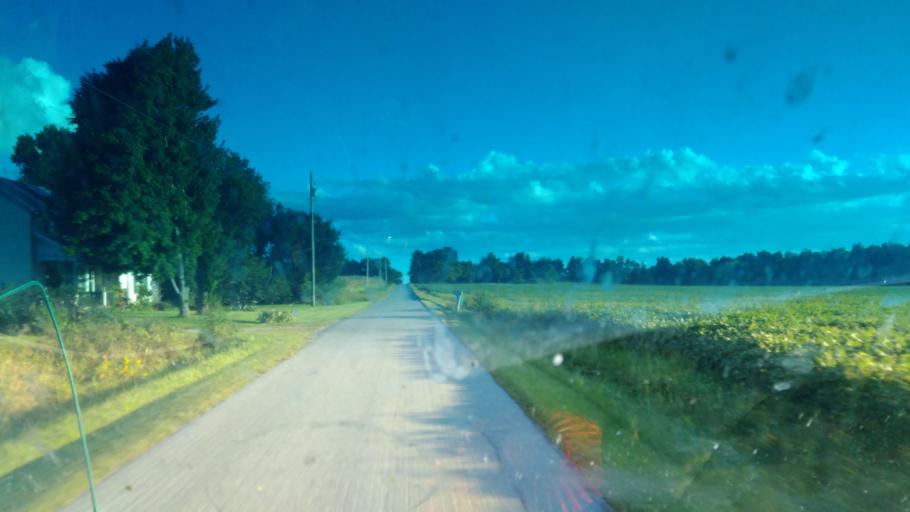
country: US
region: Ohio
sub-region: Wyandot County
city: Upper Sandusky
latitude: 40.8584
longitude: -83.1507
